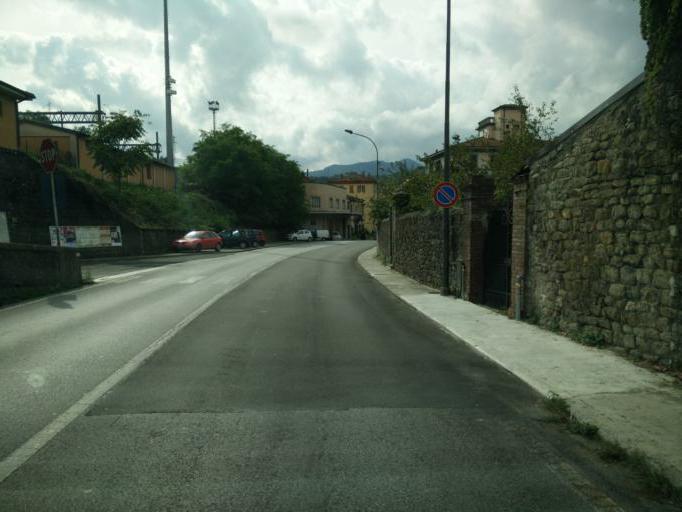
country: IT
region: Tuscany
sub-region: Provincia di Massa-Carrara
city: Pontremoli
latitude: 44.3712
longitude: 9.8871
